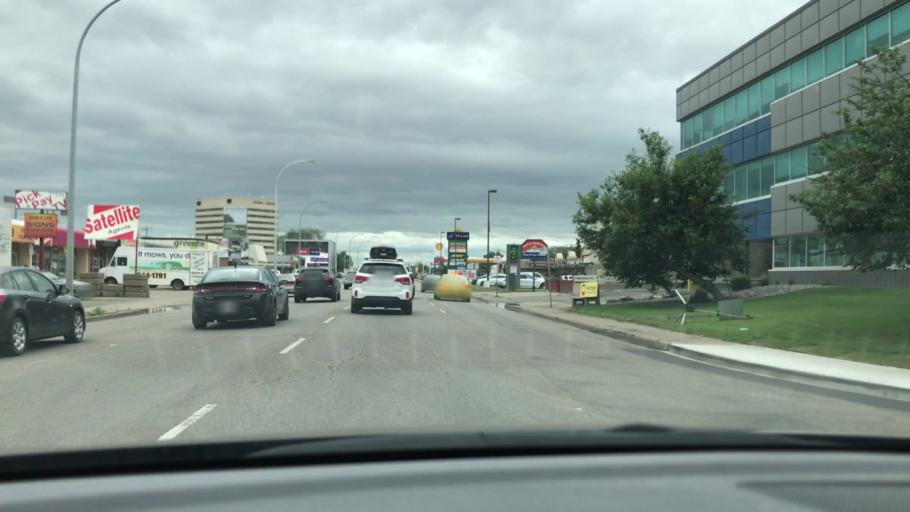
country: CA
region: Alberta
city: Edmonton
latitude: 53.4979
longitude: -113.4977
